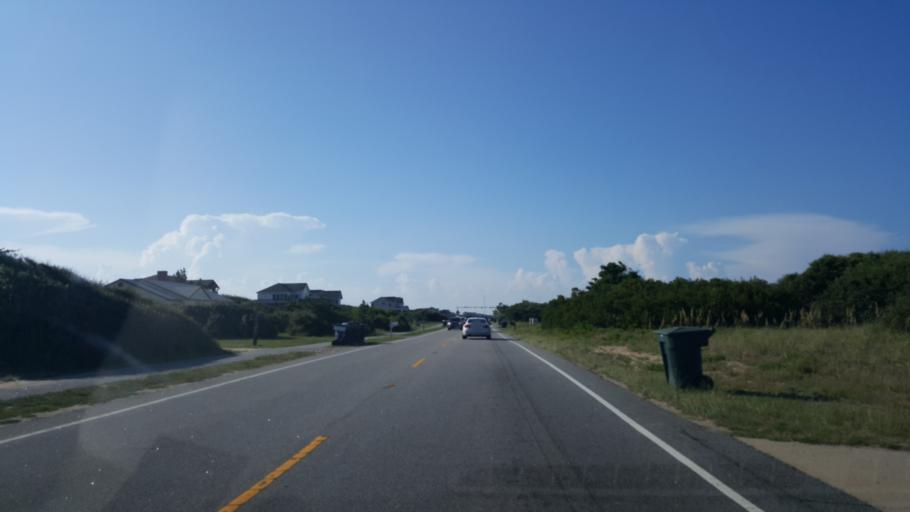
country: US
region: North Carolina
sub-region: Dare County
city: Southern Shores
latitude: 36.1115
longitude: -75.7183
